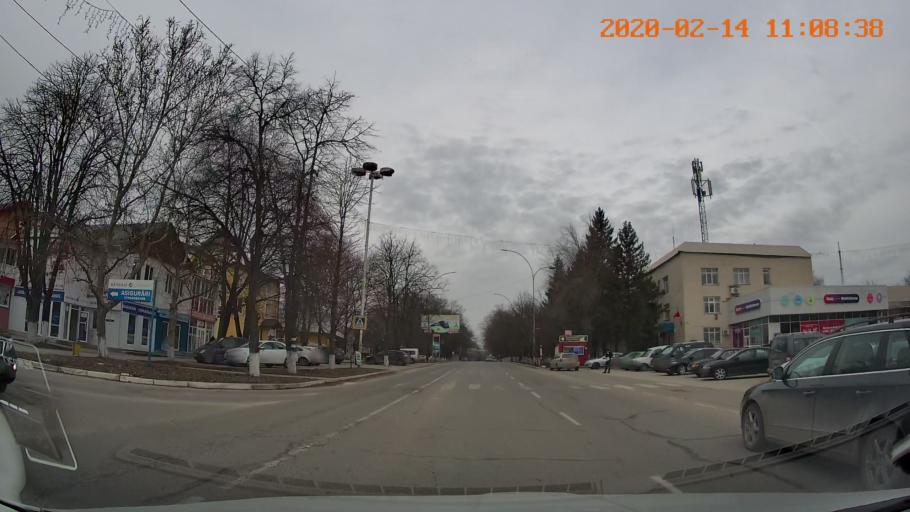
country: MD
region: Raionul Edinet
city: Edinet
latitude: 48.1731
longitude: 27.3005
